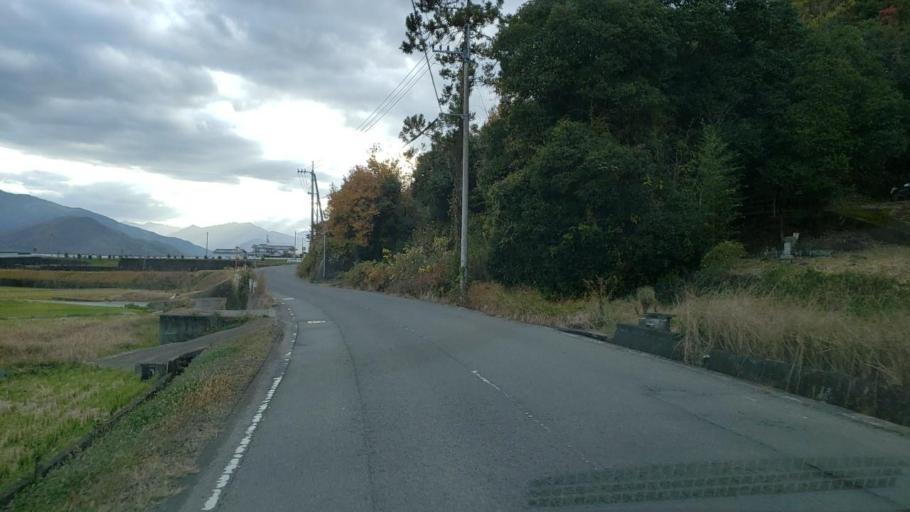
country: JP
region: Tokushima
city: Wakimachi
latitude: 34.0953
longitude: 134.2158
